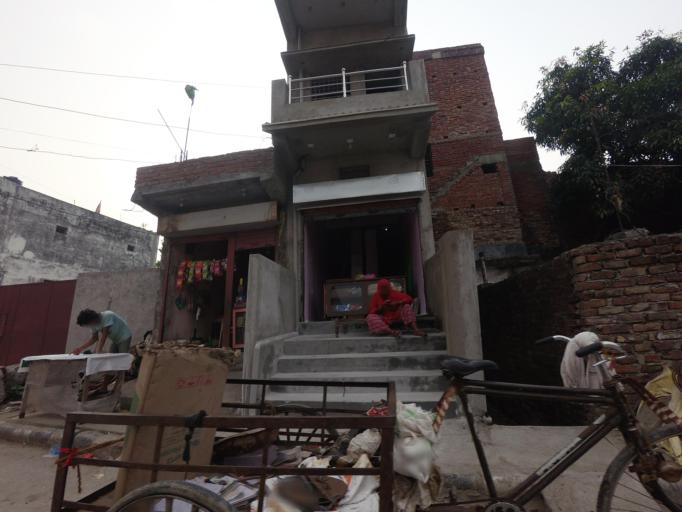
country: NP
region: Western Region
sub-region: Lumbini Zone
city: Bhairahawa
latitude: 27.5059
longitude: 83.4491
